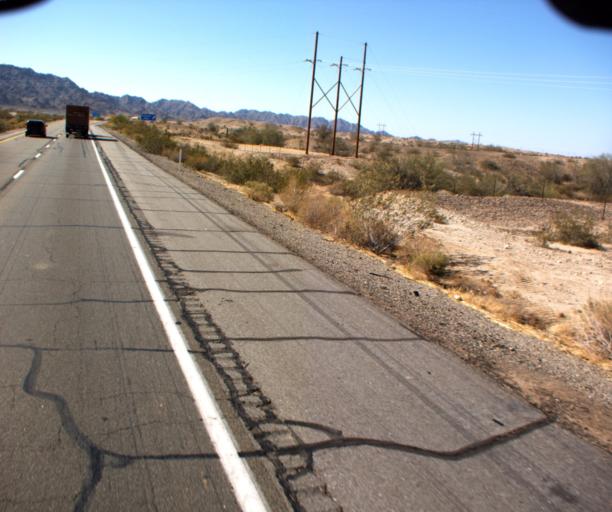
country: US
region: Arizona
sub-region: Yuma County
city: Wellton
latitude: 32.6652
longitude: -114.2755
